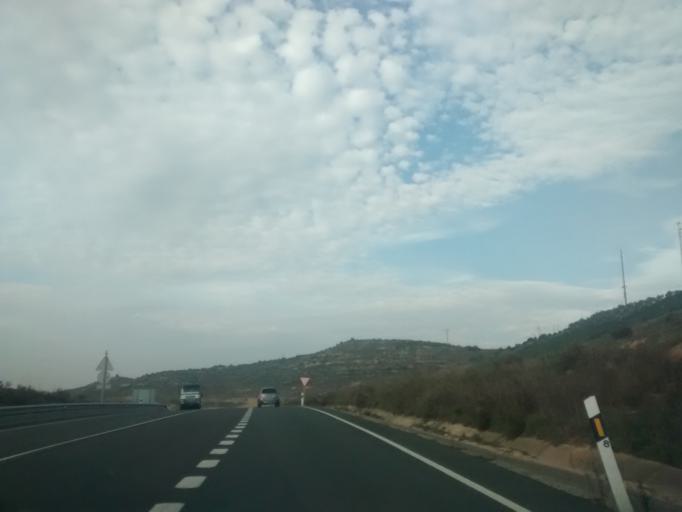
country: ES
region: La Rioja
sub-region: Provincia de La Rioja
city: Cenicero
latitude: 42.4674
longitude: -2.6224
